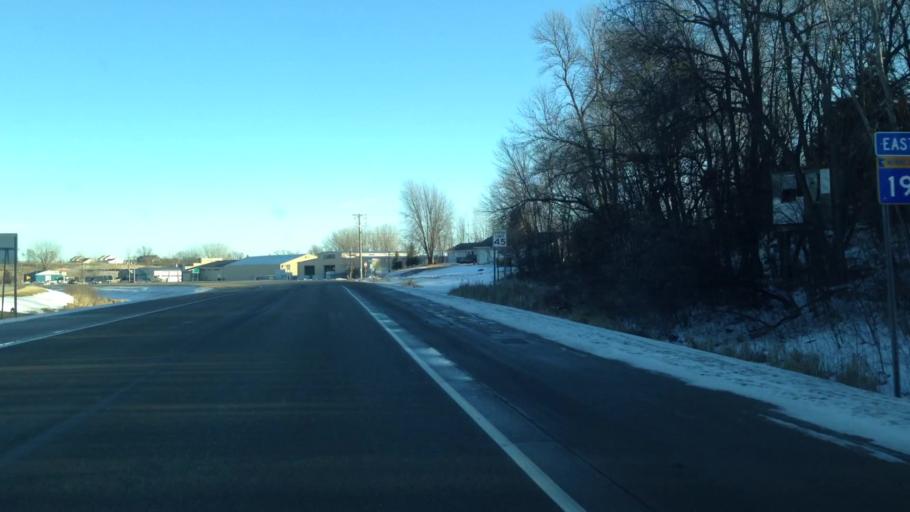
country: US
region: Minnesota
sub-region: Rice County
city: Lonsdale
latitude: 44.4799
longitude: -93.4223
